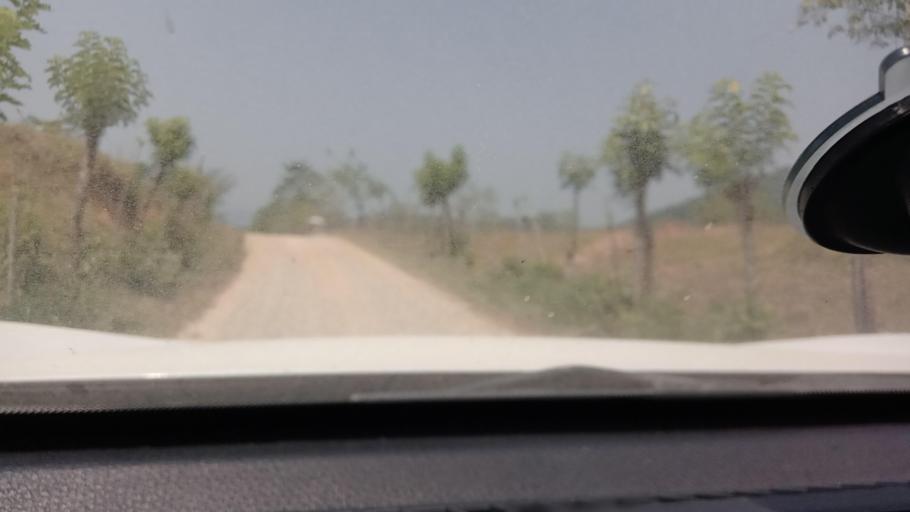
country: MX
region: Tabasco
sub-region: Huimanguillo
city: Francisco Rueda
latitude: 17.5156
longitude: -93.8920
